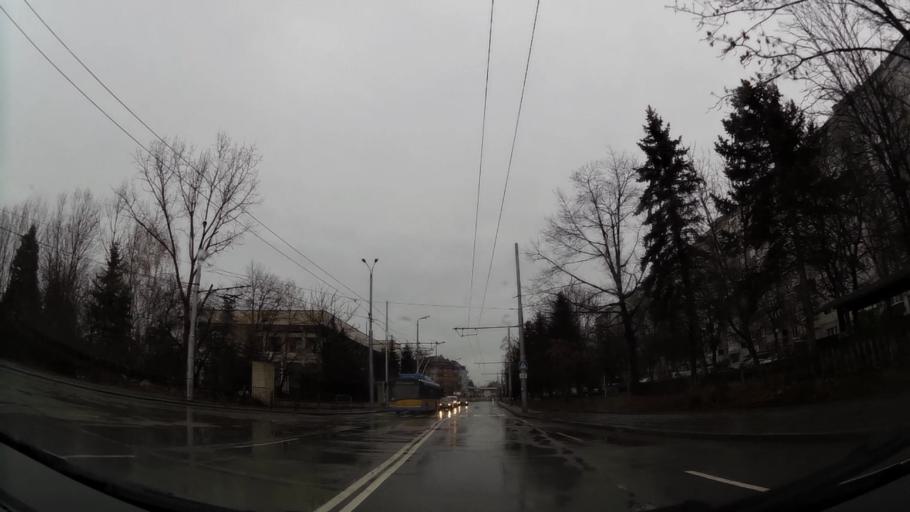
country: BG
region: Sofia-Capital
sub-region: Stolichna Obshtina
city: Sofia
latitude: 42.6513
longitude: 23.3679
